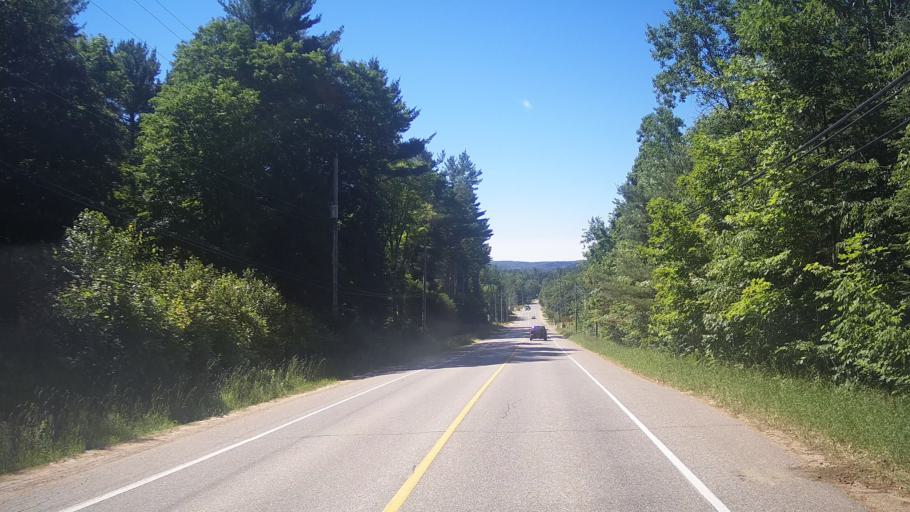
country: CA
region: Ontario
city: Huntsville
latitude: 45.3561
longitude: -79.2029
